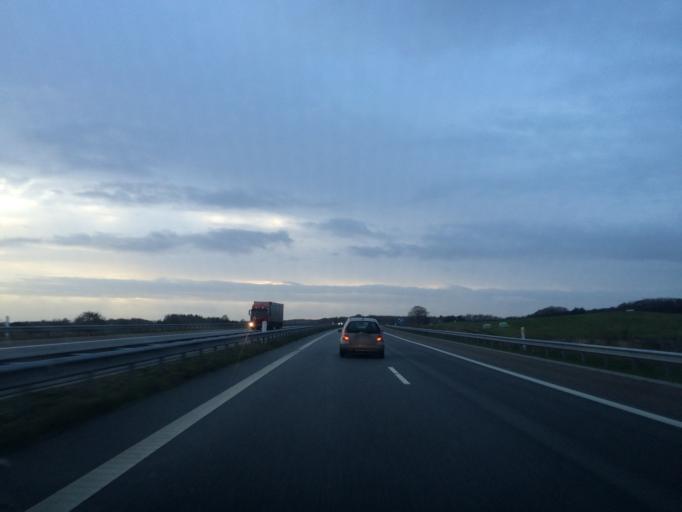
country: DK
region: South Denmark
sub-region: Aabenraa Kommune
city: Aabenraa
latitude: 54.9470
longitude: 9.4749
